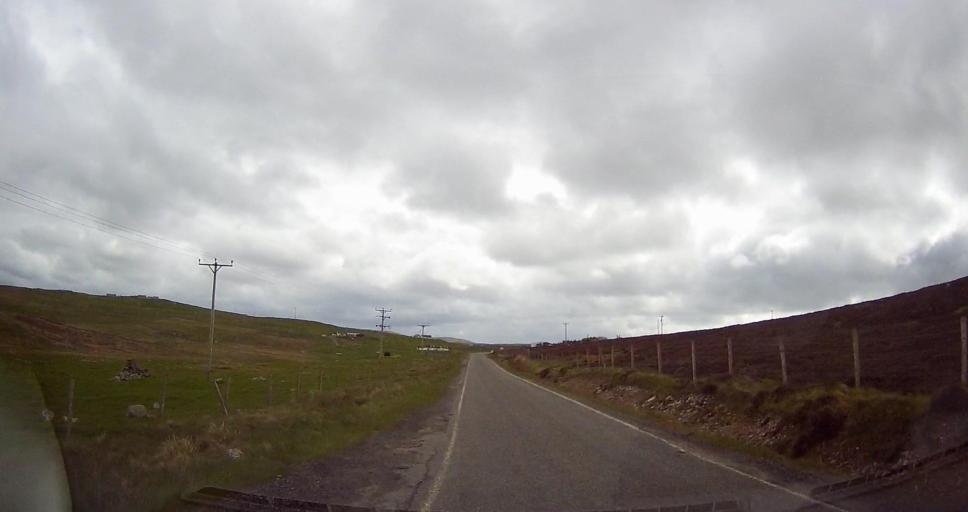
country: GB
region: Scotland
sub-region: Shetland Islands
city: Sandwick
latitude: 60.2460
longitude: -1.5109
